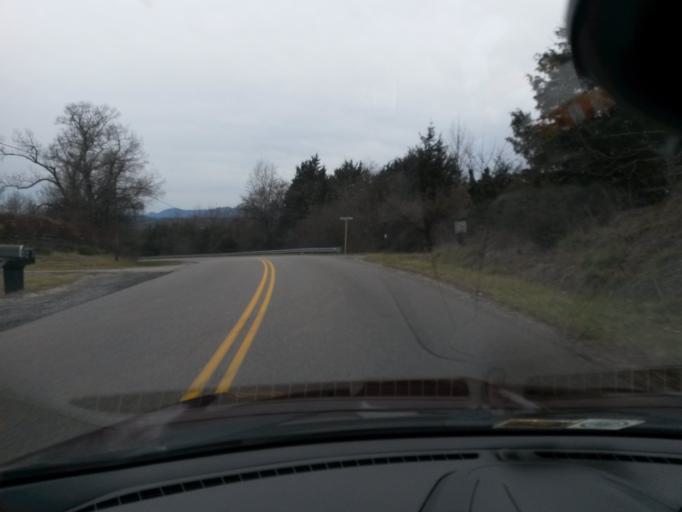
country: US
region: Virginia
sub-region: Rockbridge County
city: East Lexington
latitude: 37.7897
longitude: -79.3786
